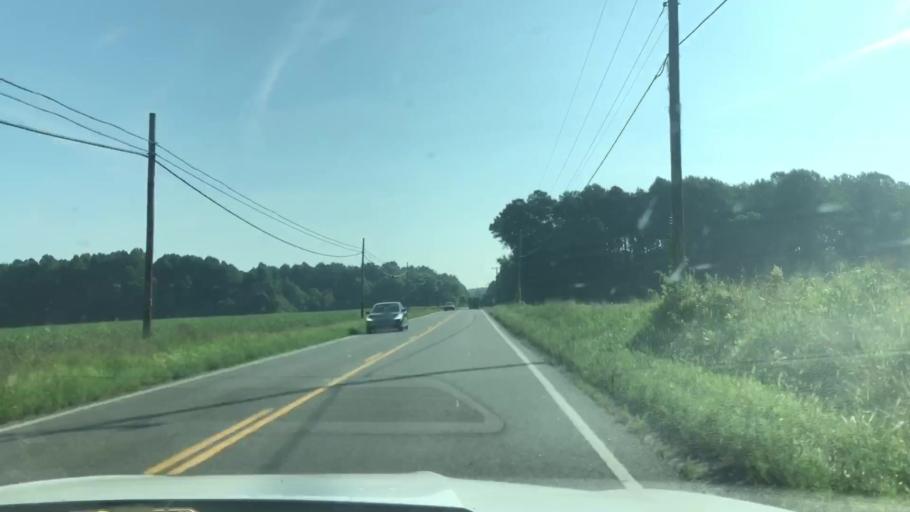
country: US
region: Virginia
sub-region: Richmond County
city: Warsaw
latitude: 37.8918
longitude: -76.6603
